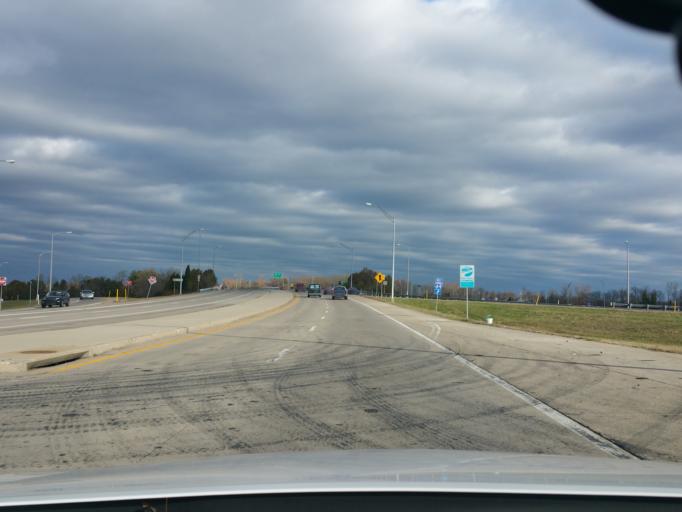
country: US
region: Kentucky
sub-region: Jefferson County
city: Douglass Hills
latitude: 38.2213
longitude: -85.5385
